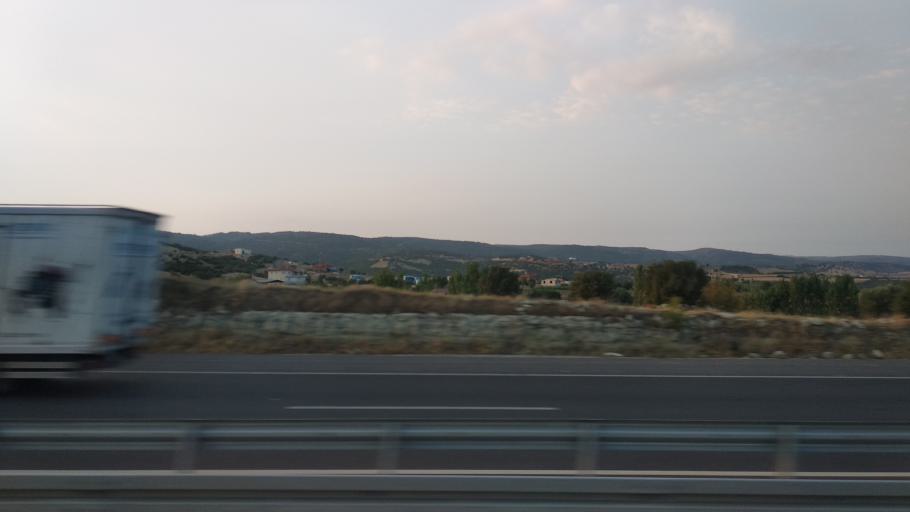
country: TR
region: Manisa
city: Selendi
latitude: 38.6224
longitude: 28.9247
